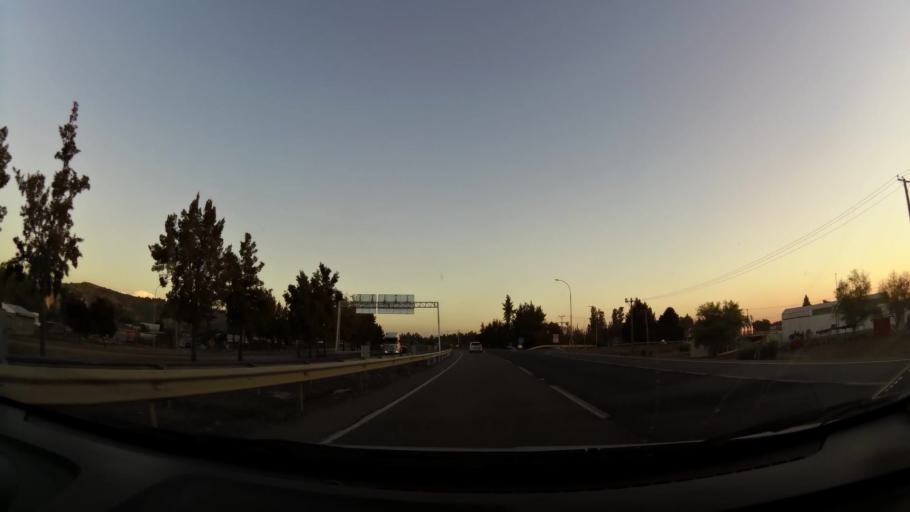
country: CL
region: Maule
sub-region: Provincia de Linares
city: Linares
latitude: -35.7611
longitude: -71.6711
